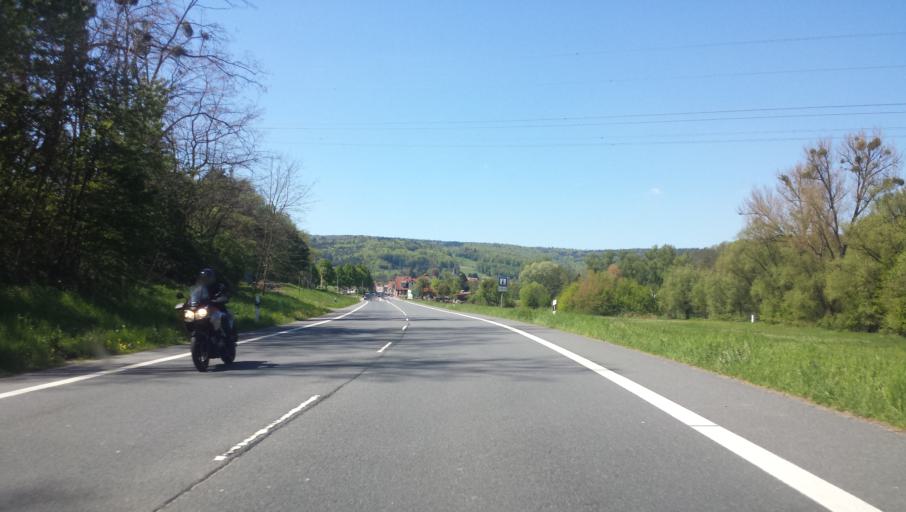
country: DE
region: Hesse
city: Reichelsheim
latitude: 49.7079
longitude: 8.8524
